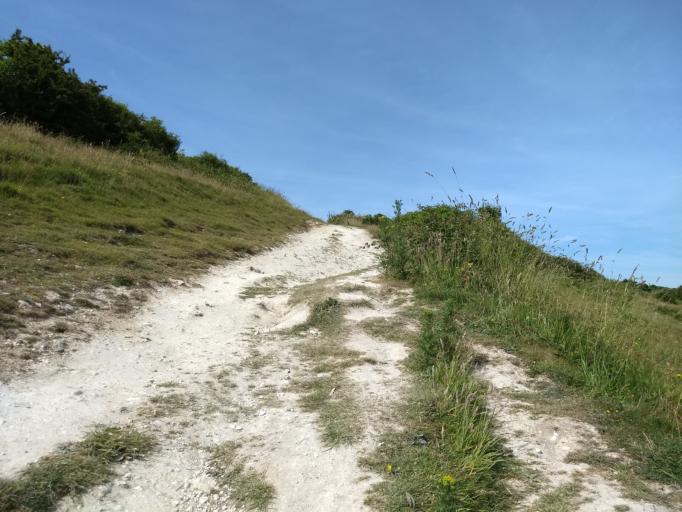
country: GB
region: England
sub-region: Isle of Wight
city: Bembridge
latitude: 50.6677
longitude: -1.1010
